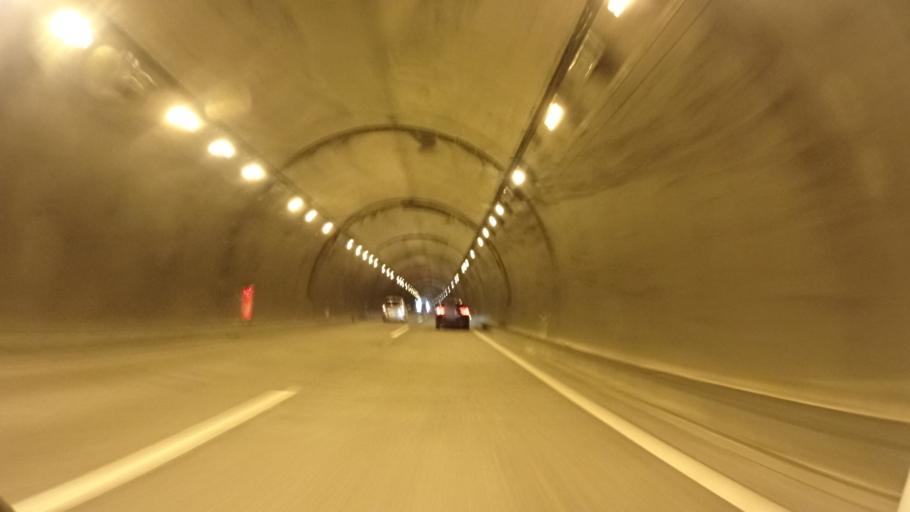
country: JP
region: Ehime
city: Niihama
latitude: 33.9195
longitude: 133.3141
